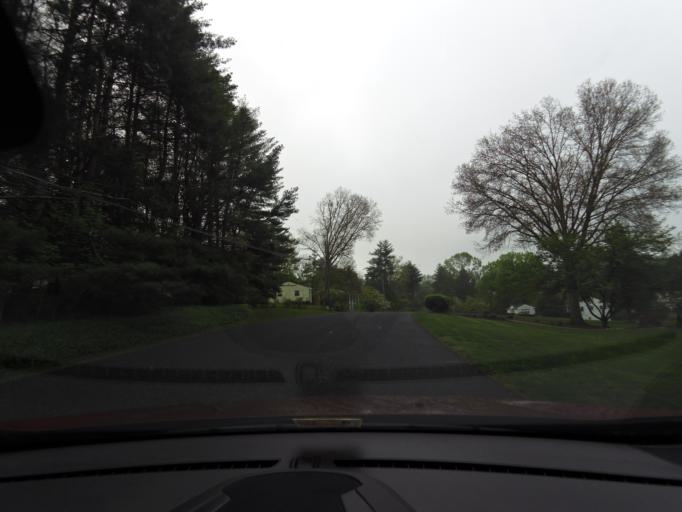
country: US
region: Virginia
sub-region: City of Lexington
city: Lexington
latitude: 37.7752
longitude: -79.4554
